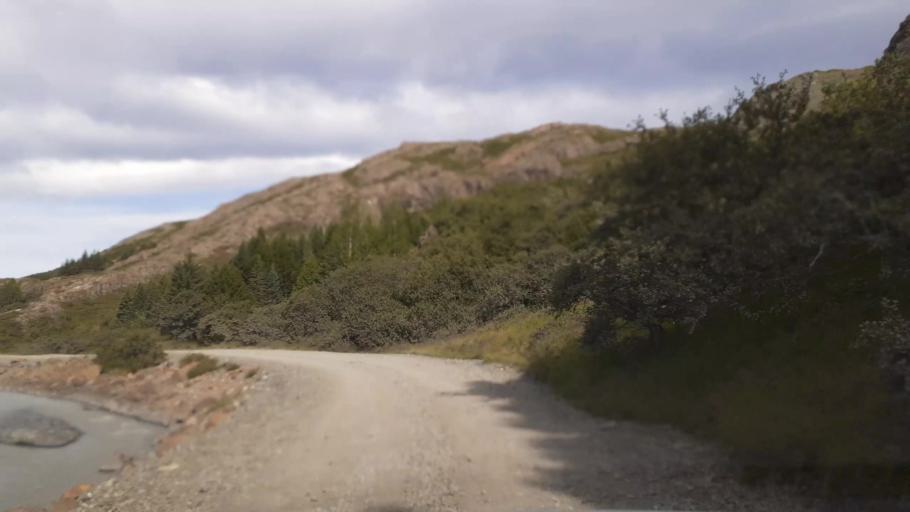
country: IS
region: East
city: Hoefn
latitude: 64.4369
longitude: -14.9083
